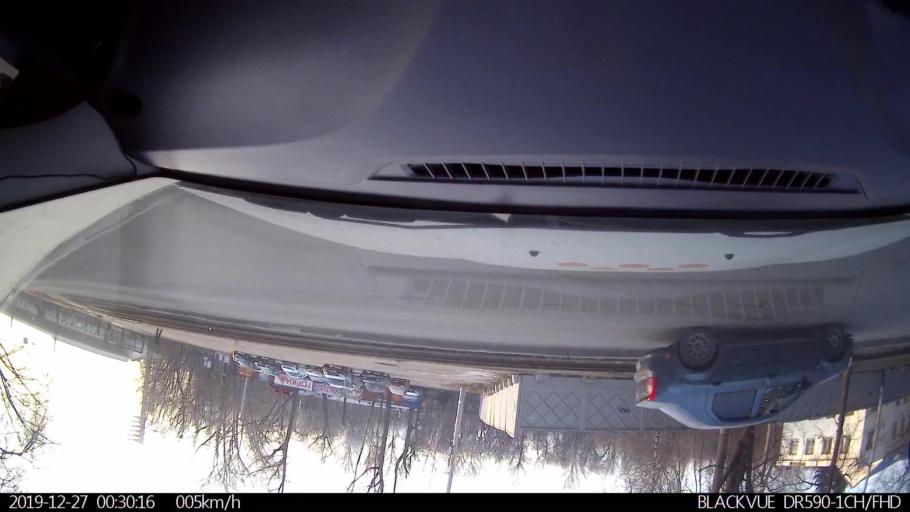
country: RU
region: Nizjnij Novgorod
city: Nizhniy Novgorod
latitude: 56.3140
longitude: 43.9314
